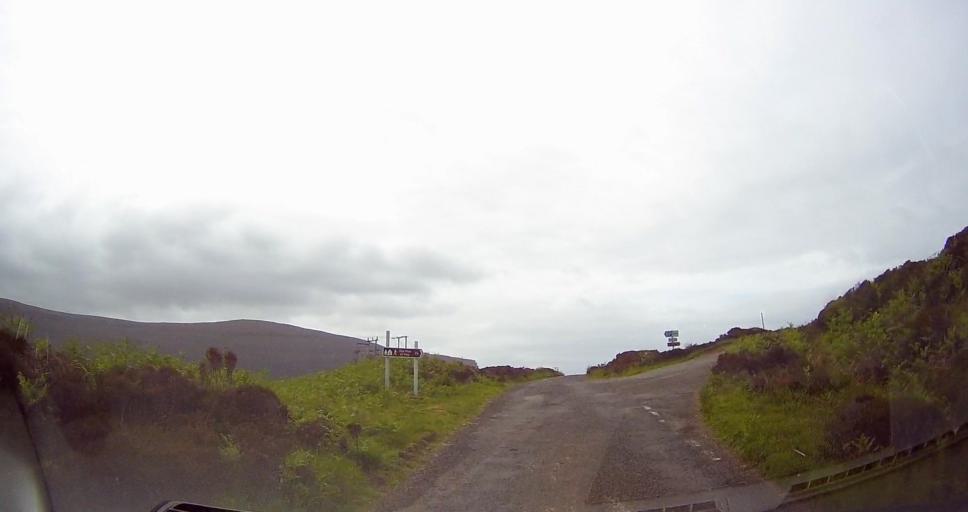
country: GB
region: Scotland
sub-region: Orkney Islands
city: Stromness
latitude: 58.8794
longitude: -3.3861
